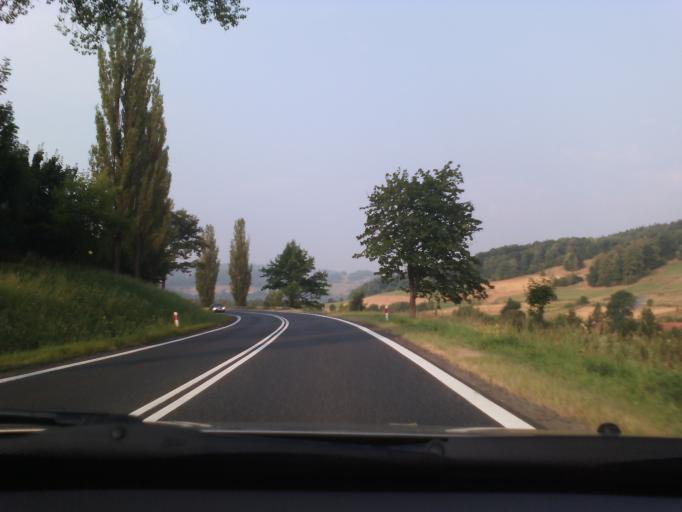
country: PL
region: Lower Silesian Voivodeship
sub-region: Powiat zlotoryjski
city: Wojcieszow
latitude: 50.9283
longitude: 15.9773
